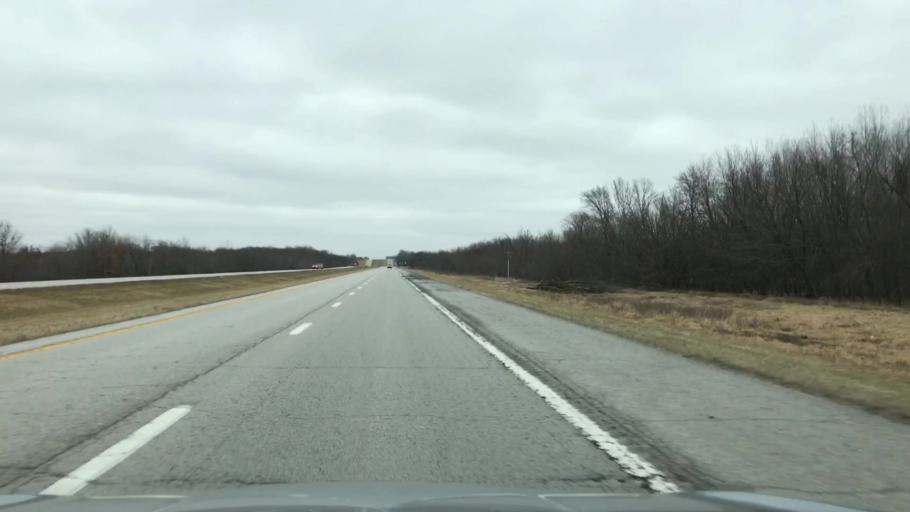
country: US
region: Missouri
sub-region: Linn County
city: Linneus
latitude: 39.7779
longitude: -93.2216
